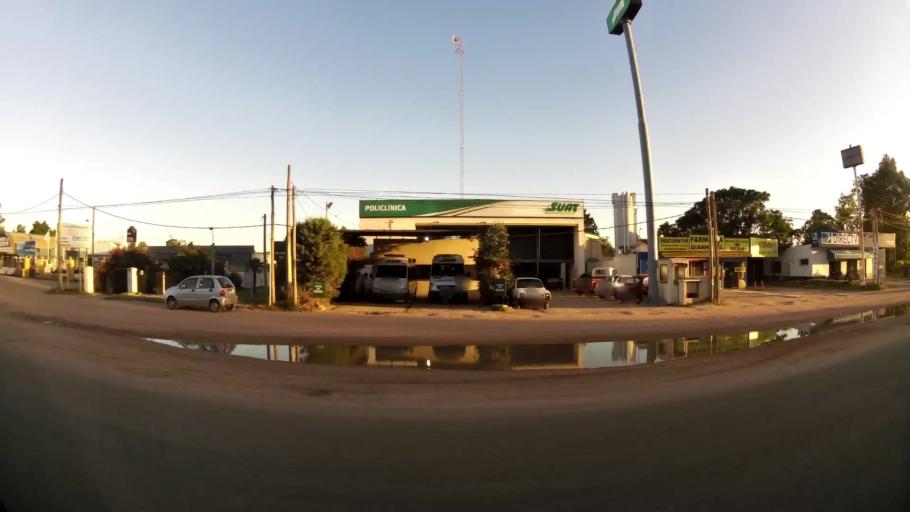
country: UY
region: Canelones
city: Barra de Carrasco
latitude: -34.8466
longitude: -56.0033
